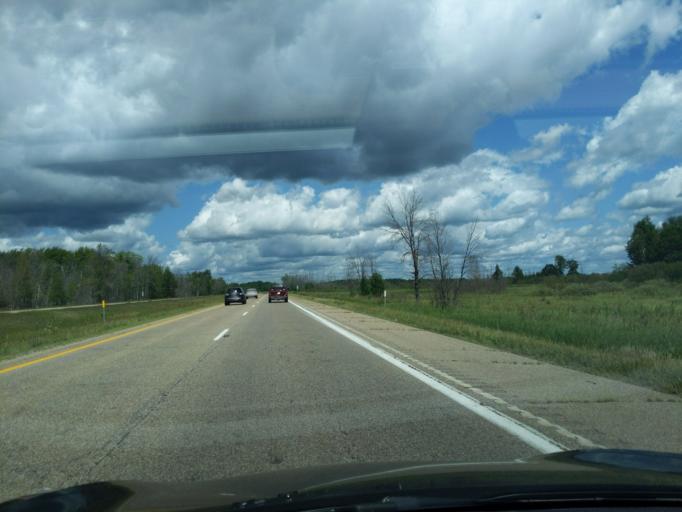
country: US
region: Michigan
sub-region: Roscommon County
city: Houghton Lake
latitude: 44.3737
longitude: -84.8079
